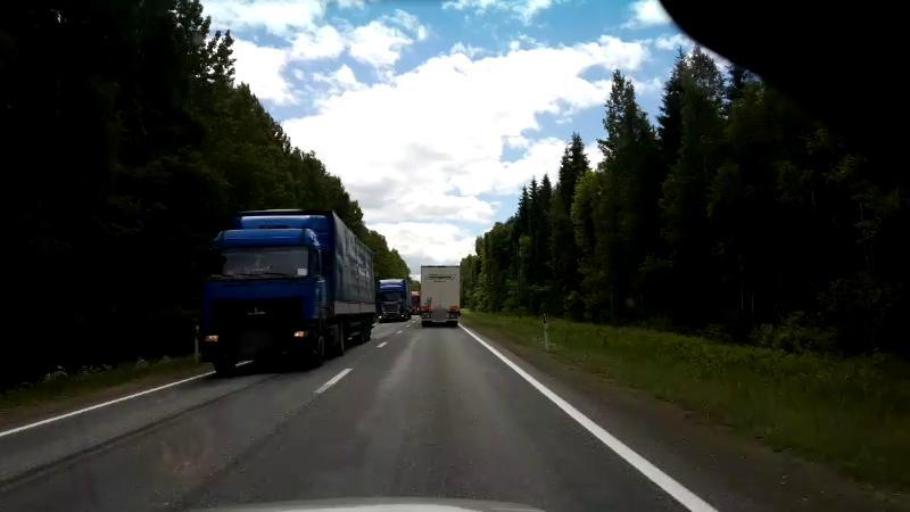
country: LV
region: Salacgrivas
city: Salacgriva
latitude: 57.5955
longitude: 24.4141
